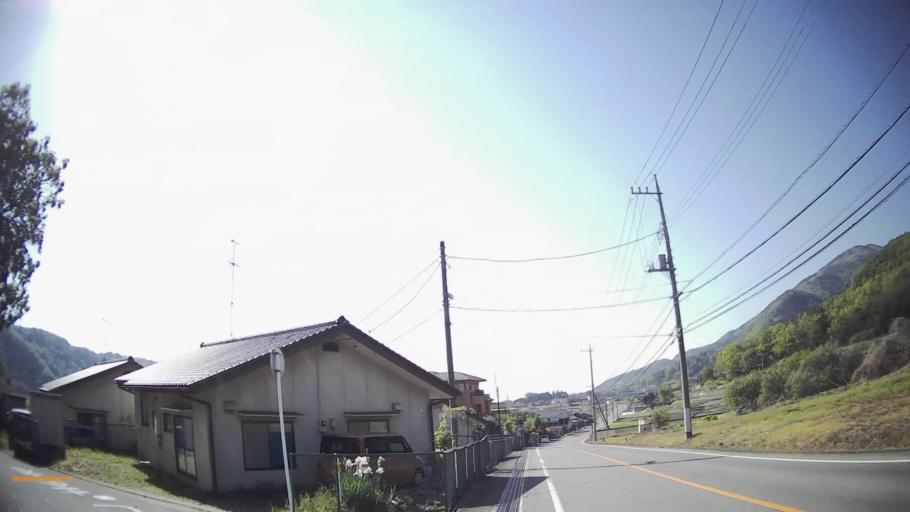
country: JP
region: Yamanashi
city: Nirasaki
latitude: 35.7397
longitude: 138.4075
